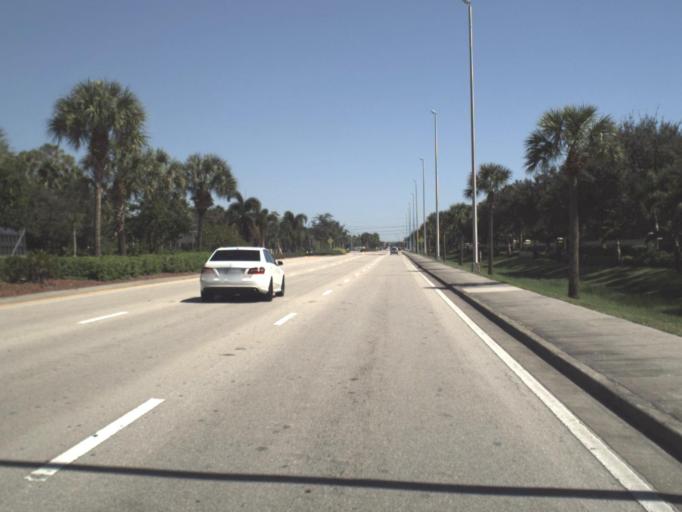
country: US
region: Florida
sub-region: Collier County
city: Pine Ridge
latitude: 26.2116
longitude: -81.7586
